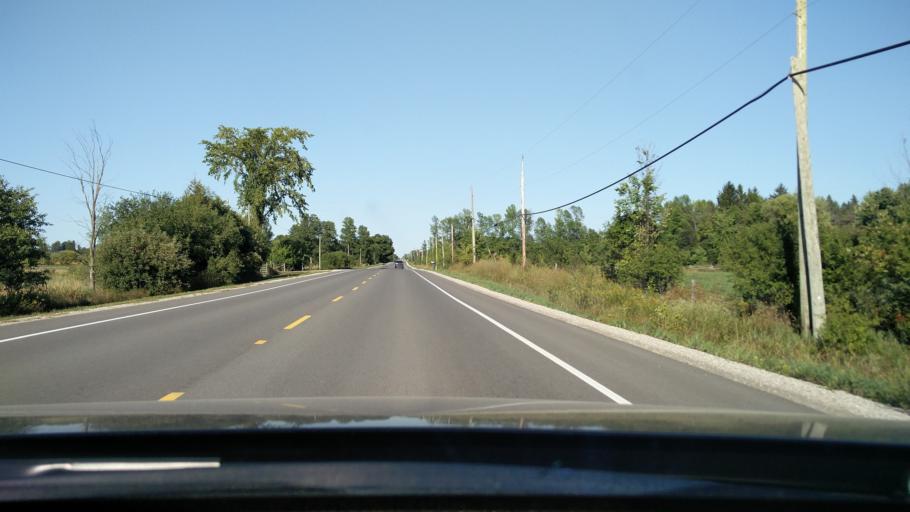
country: CA
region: Ontario
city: Perth
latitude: 44.9219
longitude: -76.2192
